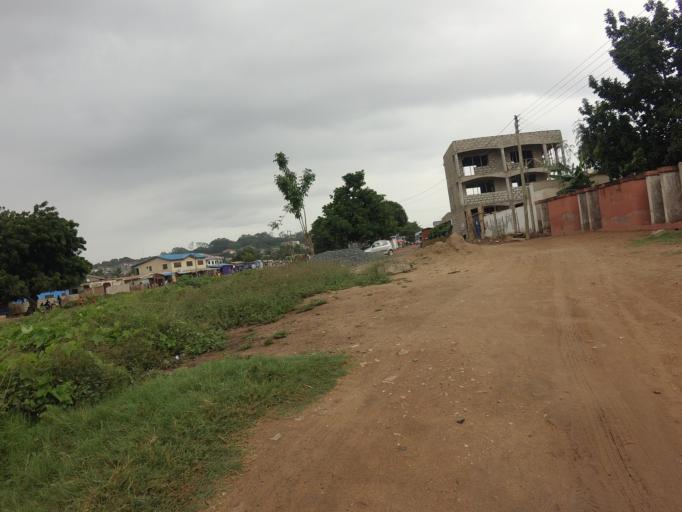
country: GH
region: Greater Accra
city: Dome
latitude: 5.6333
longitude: -0.2301
